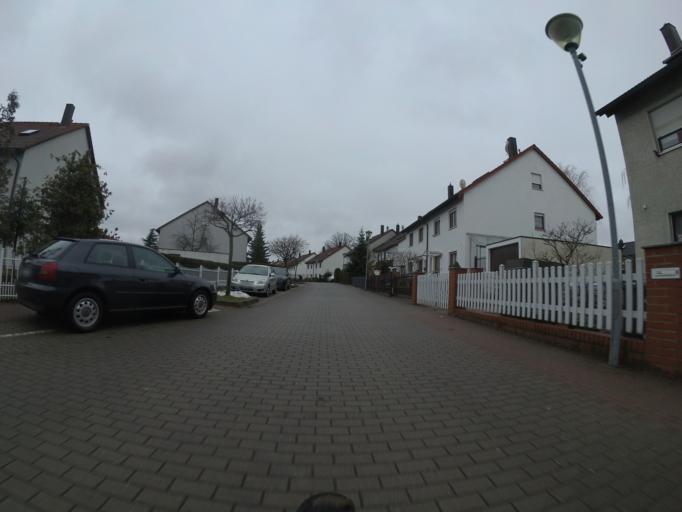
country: DE
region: Berlin
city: Marzahn
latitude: 52.5507
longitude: 13.5895
